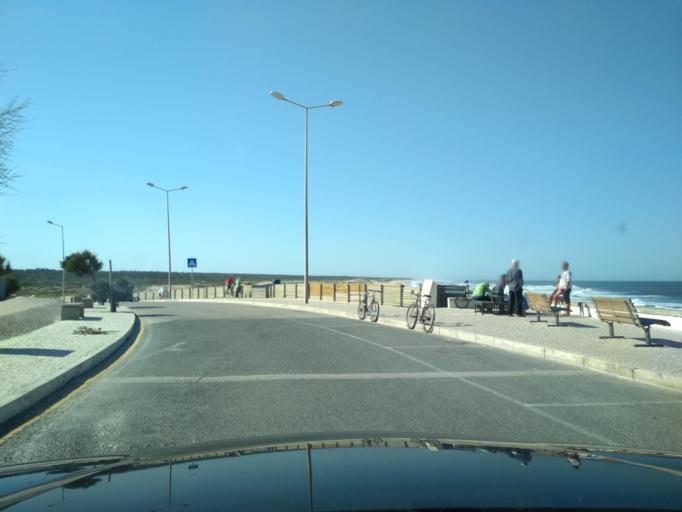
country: PT
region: Coimbra
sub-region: Figueira da Foz
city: Lavos
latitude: 40.0559
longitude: -8.8908
